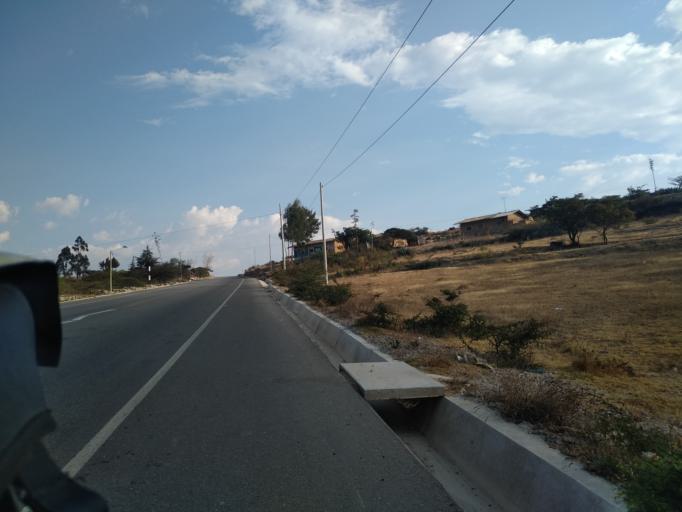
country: PE
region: Cajamarca
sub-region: San Marcos
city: La Grama
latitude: -7.3989
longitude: -78.1256
